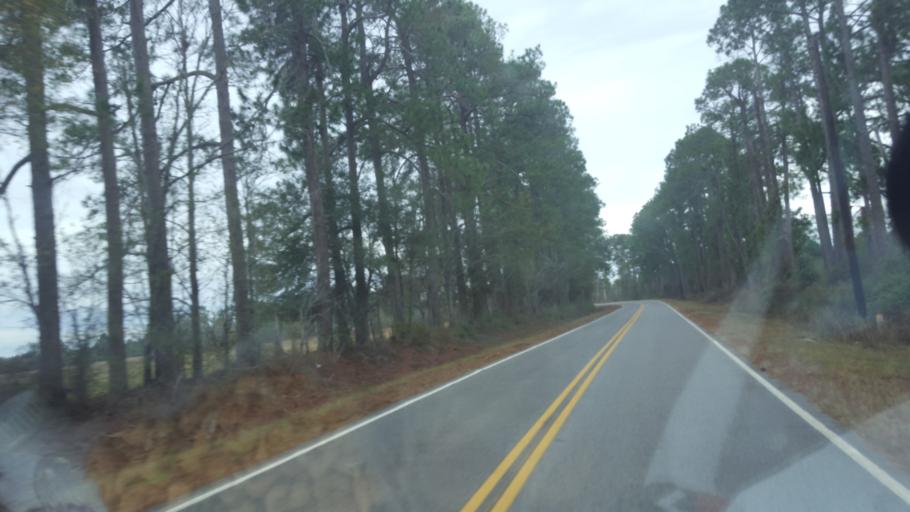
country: US
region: Georgia
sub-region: Wilcox County
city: Rochelle
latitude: 31.8123
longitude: -83.4612
